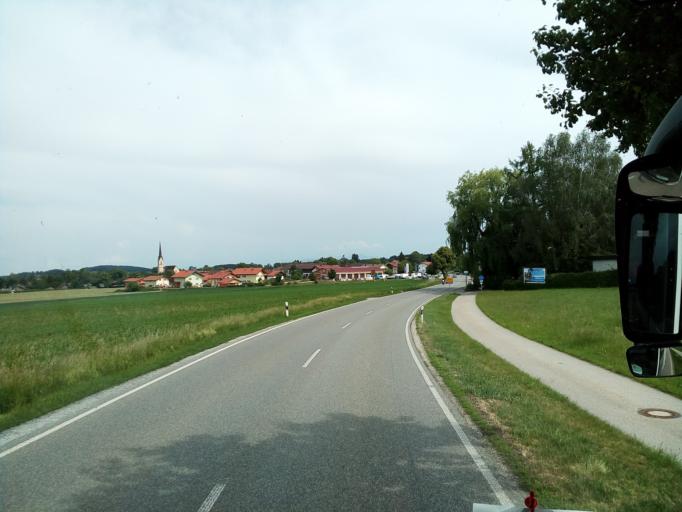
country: DE
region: Bavaria
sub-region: Upper Bavaria
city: Obing
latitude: 48.0044
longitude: 12.3978
